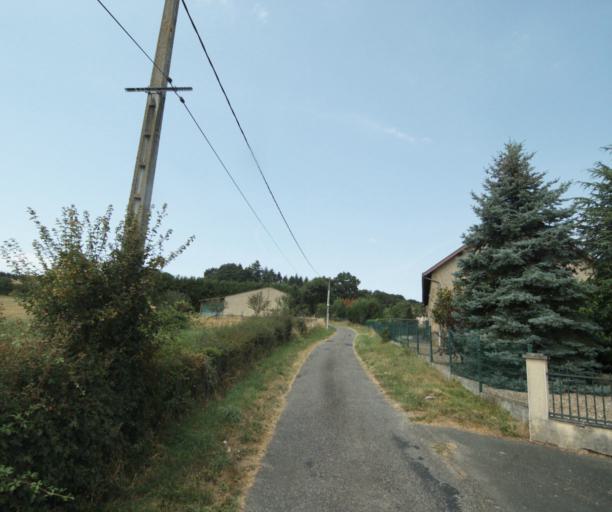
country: FR
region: Bourgogne
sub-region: Departement de Saone-et-Loire
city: Gueugnon
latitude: 46.6048
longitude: 4.0364
